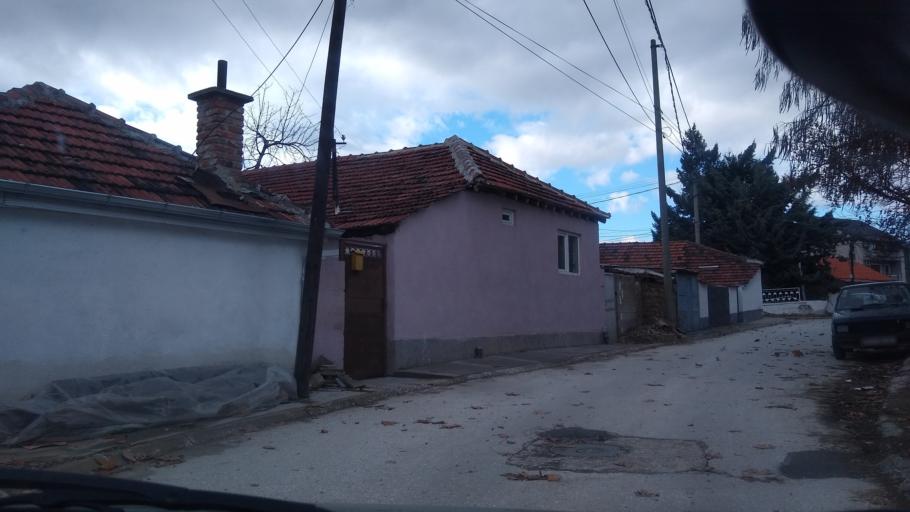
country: MK
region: Bitola
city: Bitola
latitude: 41.0240
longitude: 21.3278
